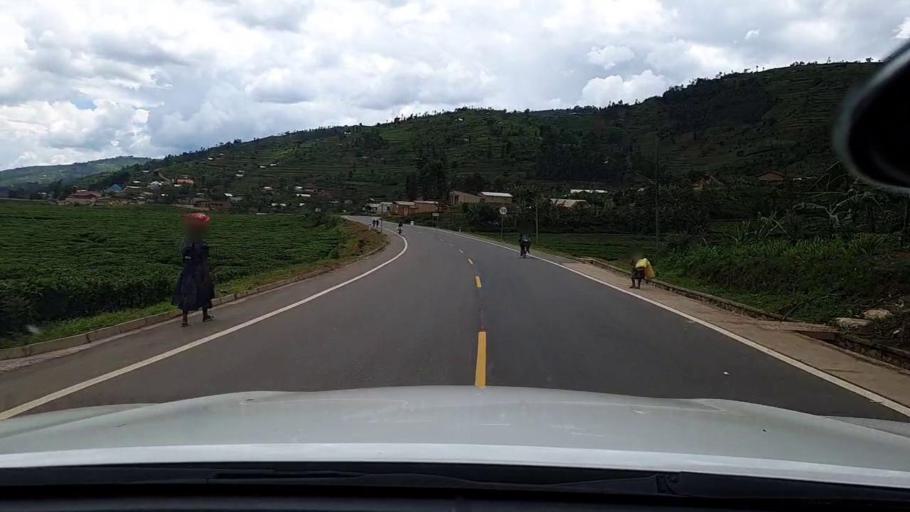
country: RW
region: Northern Province
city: Byumba
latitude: -1.6498
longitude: 29.9022
